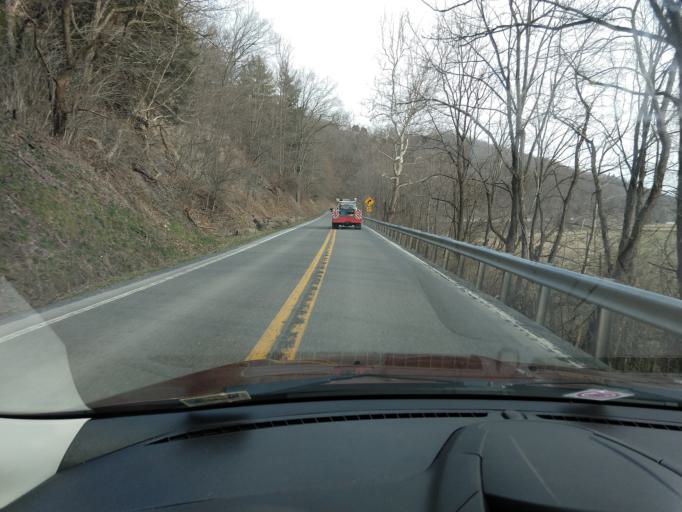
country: US
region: West Virginia
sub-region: Pendleton County
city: Franklin
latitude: 38.6205
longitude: -79.3435
